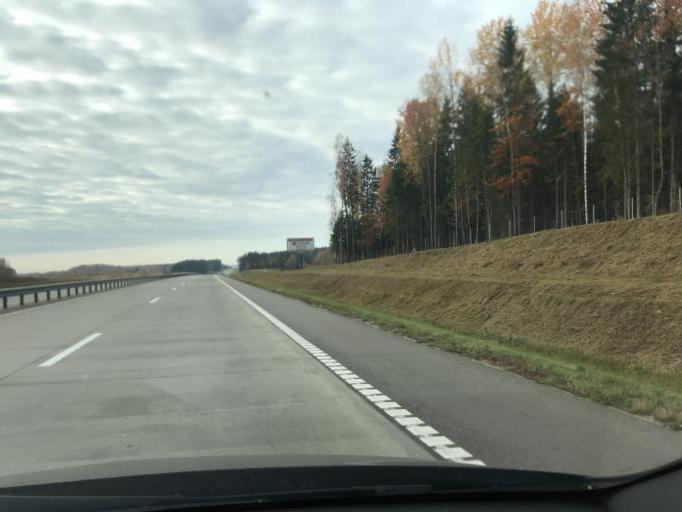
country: BY
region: Minsk
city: Rakaw
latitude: 54.0115
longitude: 27.1340
